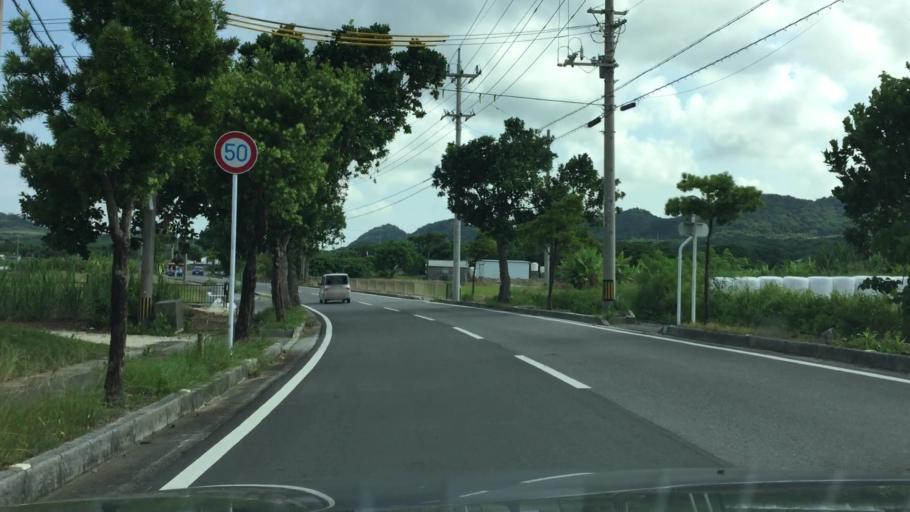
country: JP
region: Okinawa
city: Ishigaki
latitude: 24.4591
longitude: 124.2494
